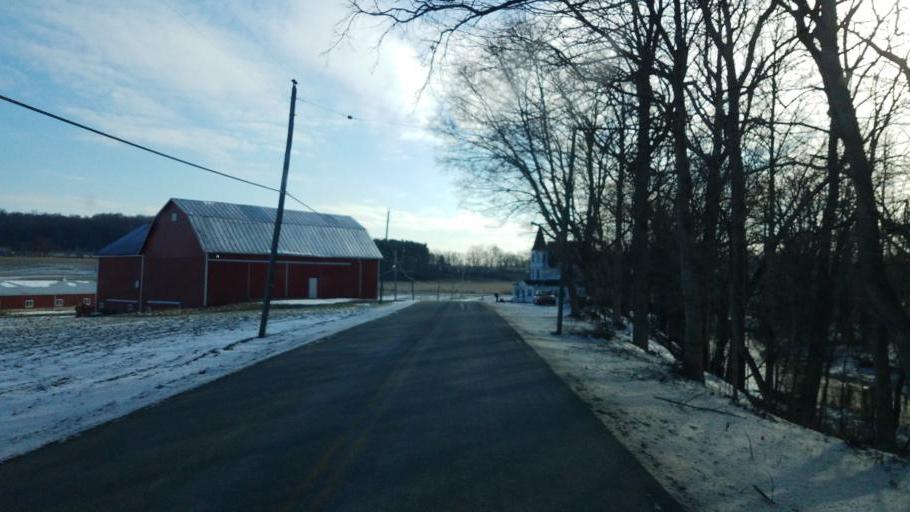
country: US
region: Ohio
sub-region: Richland County
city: Lexington
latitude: 40.6183
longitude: -82.5845
